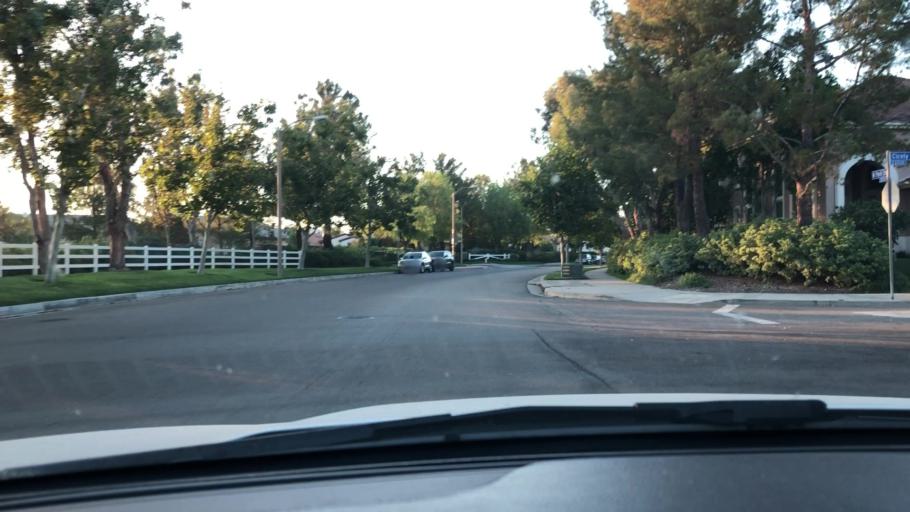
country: US
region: California
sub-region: Los Angeles County
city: Santa Clarita
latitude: 34.4561
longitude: -118.5447
